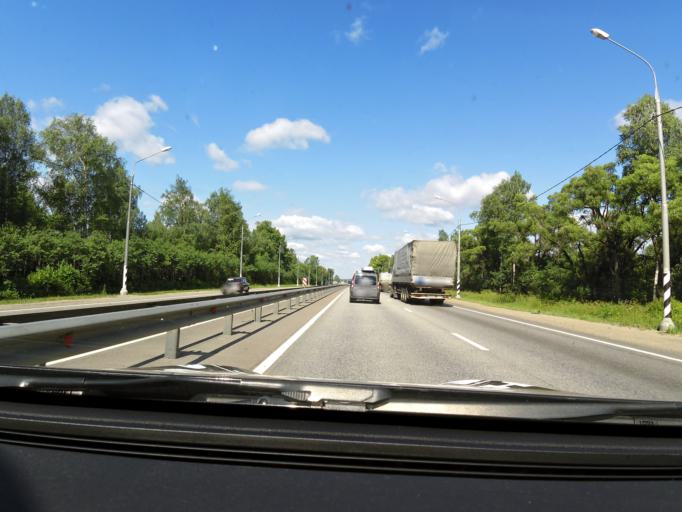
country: RU
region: Tverskaya
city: Likhoslavl'
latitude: 56.9684
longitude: 35.3141
